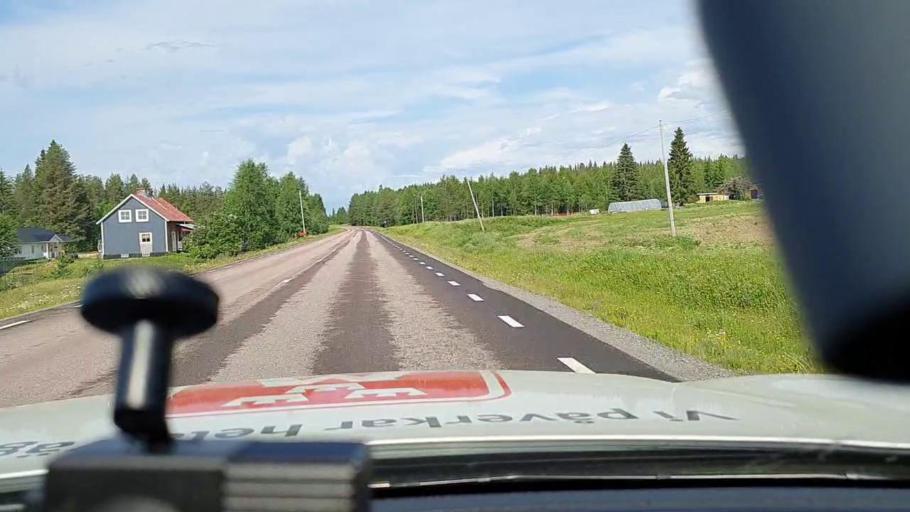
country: SE
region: Norrbotten
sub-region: Alvsbyns Kommun
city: AElvsbyn
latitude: 66.0206
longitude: 21.1373
